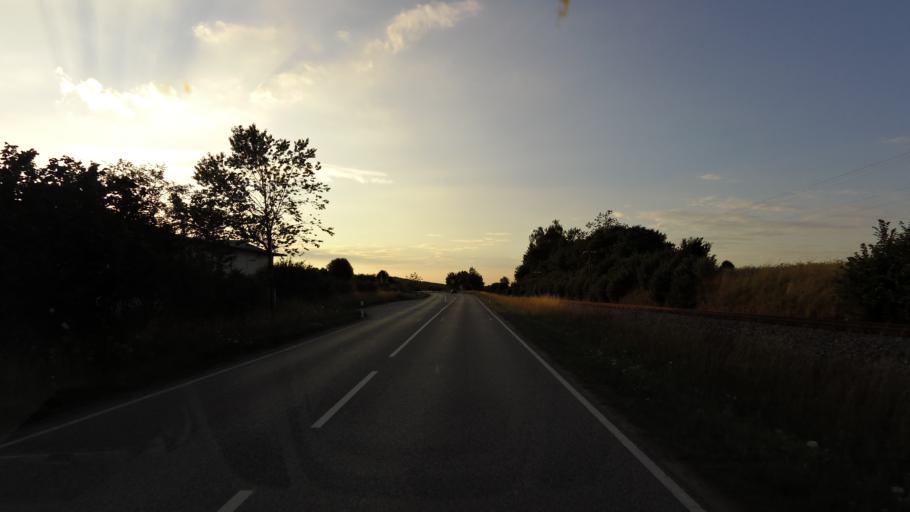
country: DE
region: Bavaria
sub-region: Upper Bavaria
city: Nussdorf
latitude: 47.9047
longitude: 12.6167
